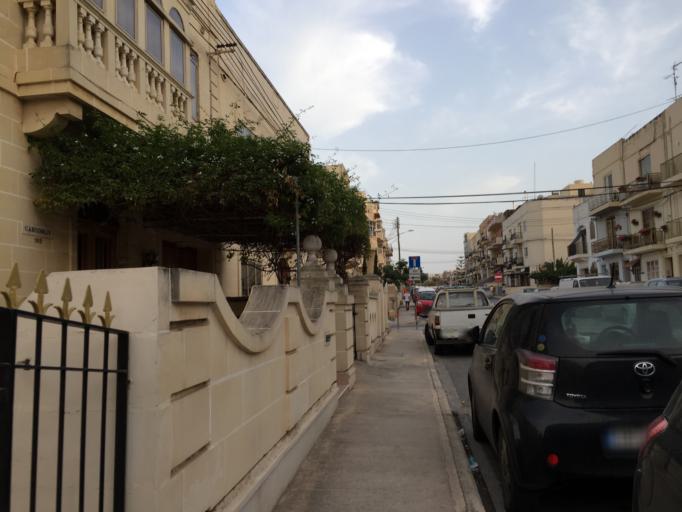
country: MT
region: Il-Fgura
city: Fgura
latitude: 35.8740
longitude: 14.5218
